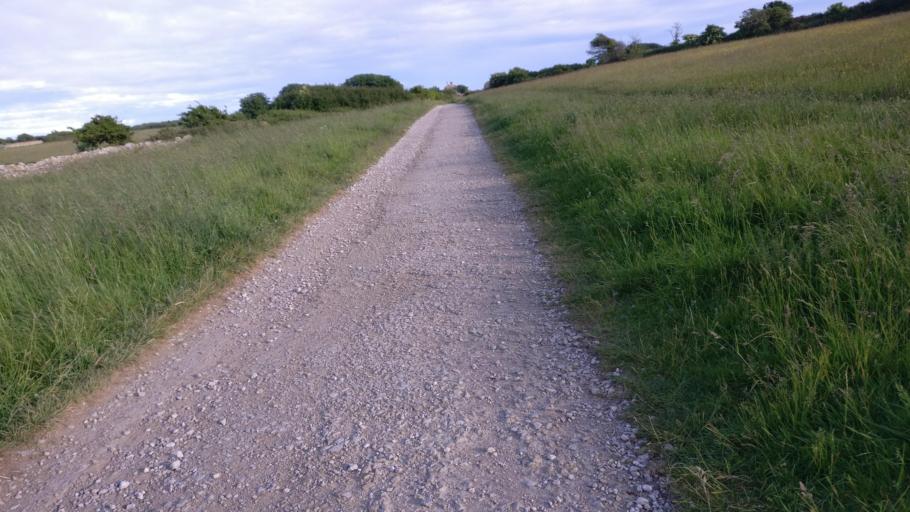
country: GB
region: England
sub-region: Dorset
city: Swanage
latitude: 50.6025
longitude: -2.0040
